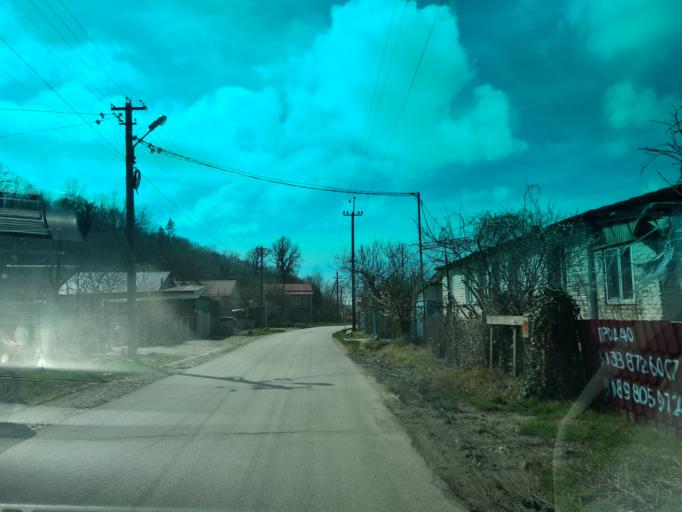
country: RU
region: Krasnodarskiy
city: Shepsi
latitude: 44.0489
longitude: 39.1591
